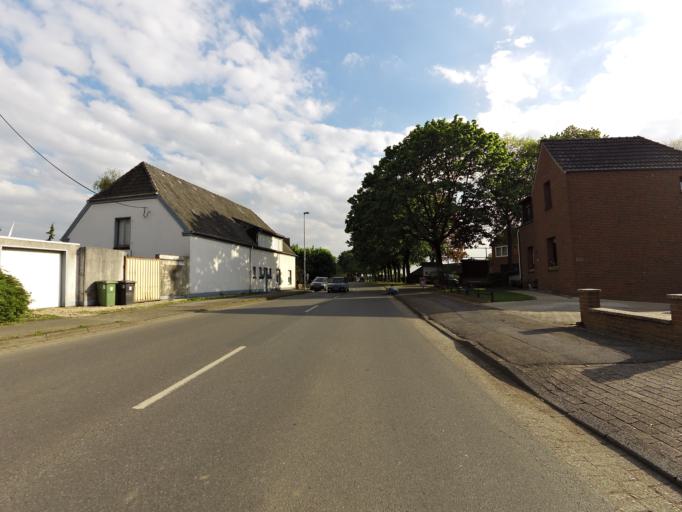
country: DE
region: North Rhine-Westphalia
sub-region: Regierungsbezirk Dusseldorf
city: Kleve
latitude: 51.8206
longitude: 6.1656
